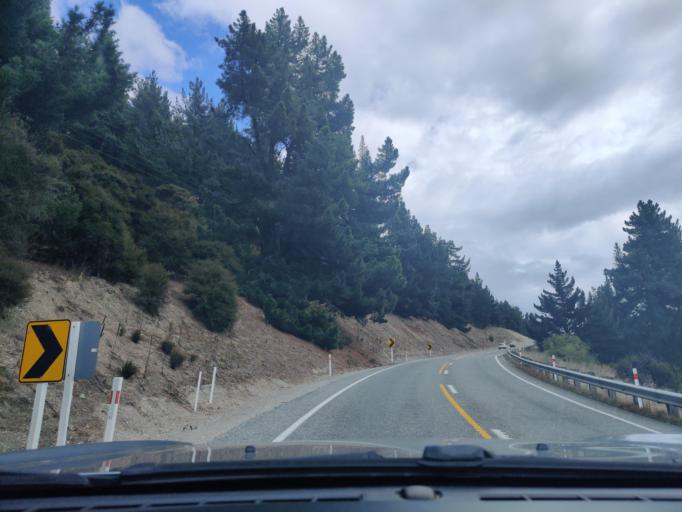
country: NZ
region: Otago
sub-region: Queenstown-Lakes District
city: Wanaka
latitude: -44.7326
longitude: 169.2559
